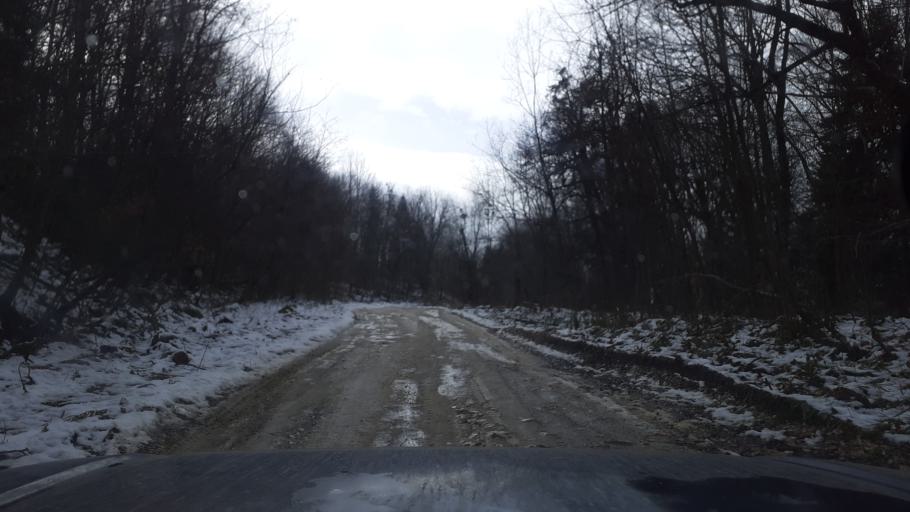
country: RU
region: Krasnodarskiy
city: Neftegorsk
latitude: 44.0743
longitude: 39.7580
